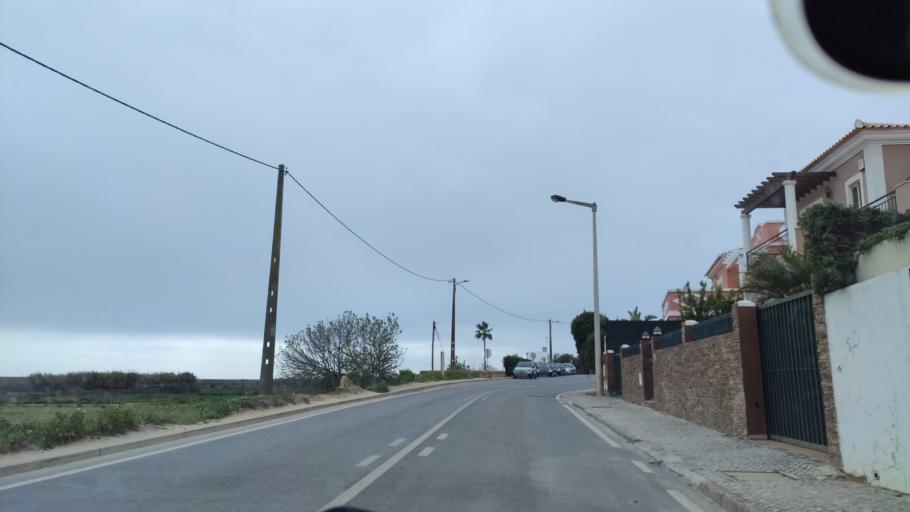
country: PT
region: Faro
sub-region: Faro
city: Faro
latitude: 37.0325
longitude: -7.9555
